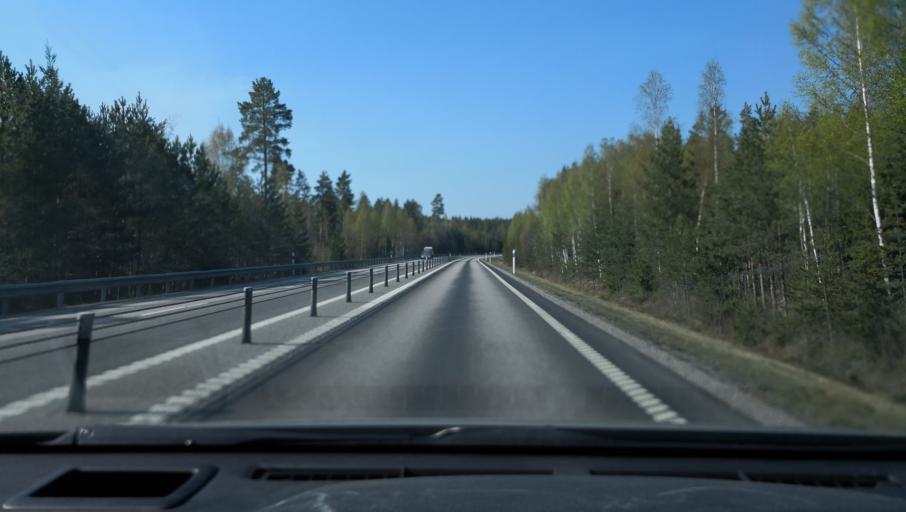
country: SE
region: Uppsala
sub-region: Heby Kommun
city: Tarnsjo
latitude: 60.1785
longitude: 16.9480
